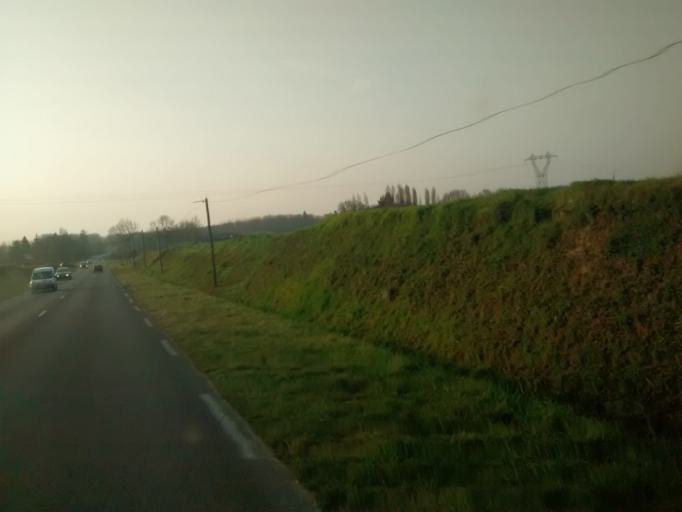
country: FR
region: Brittany
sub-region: Departement d'Ille-et-Vilaine
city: Chavagne
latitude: 48.0640
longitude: -1.8138
